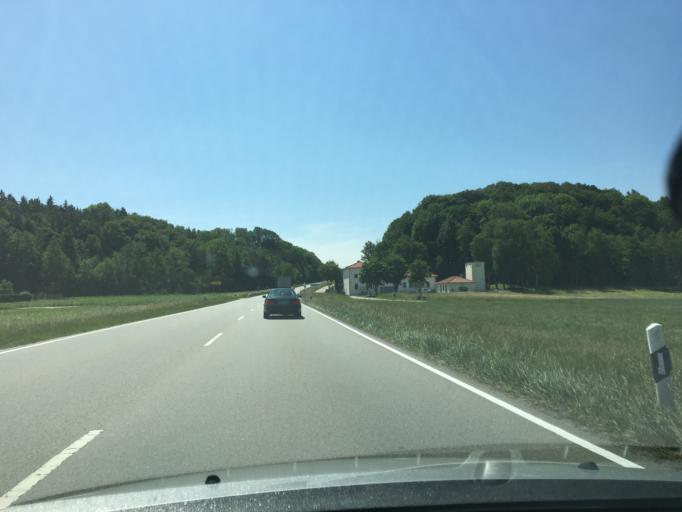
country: DE
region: Bavaria
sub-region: Upper Bavaria
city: Altoetting
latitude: 48.2132
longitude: 12.6561
